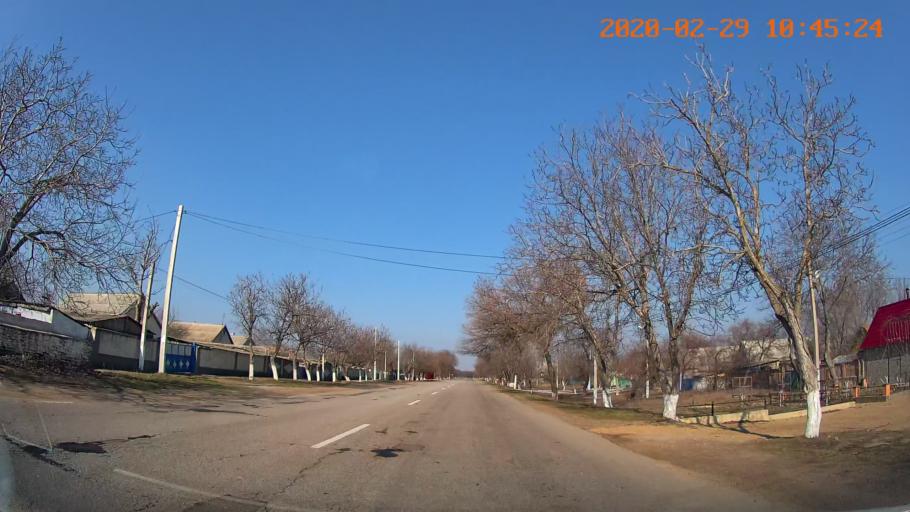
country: MD
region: Telenesti
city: Grigoriopol
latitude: 47.0754
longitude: 29.3836
